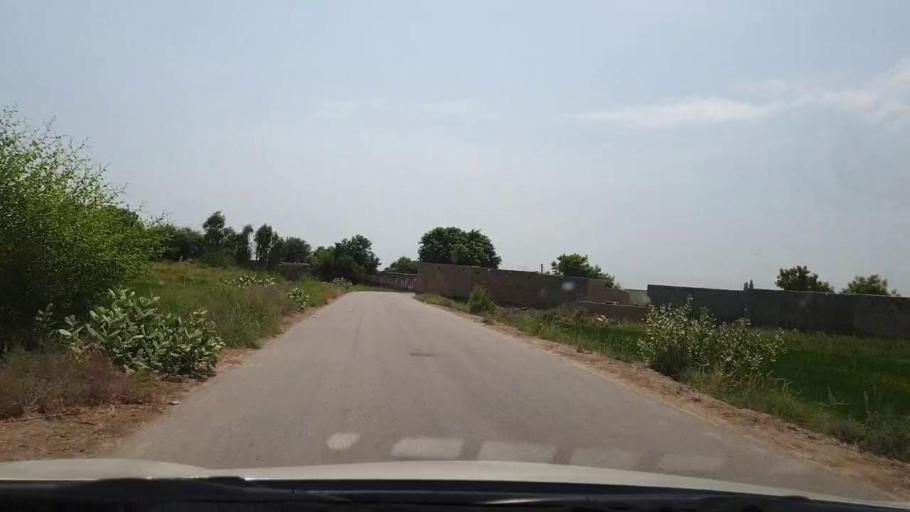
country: PK
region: Sindh
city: Ratodero
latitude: 27.8132
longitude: 68.2502
